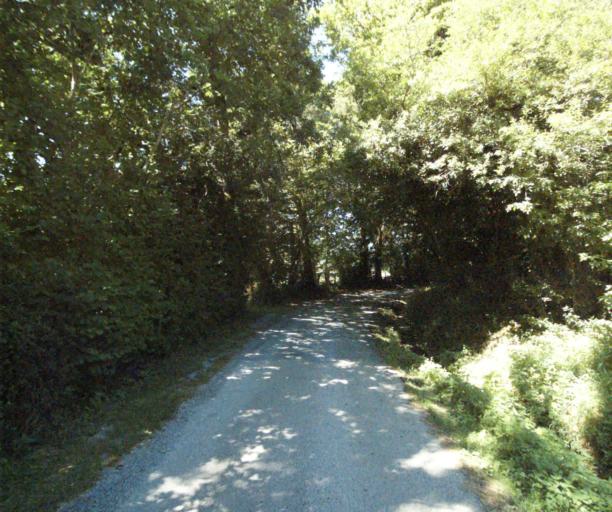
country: FR
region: Midi-Pyrenees
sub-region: Departement du Tarn
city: Dourgne
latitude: 43.4422
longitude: 2.1984
